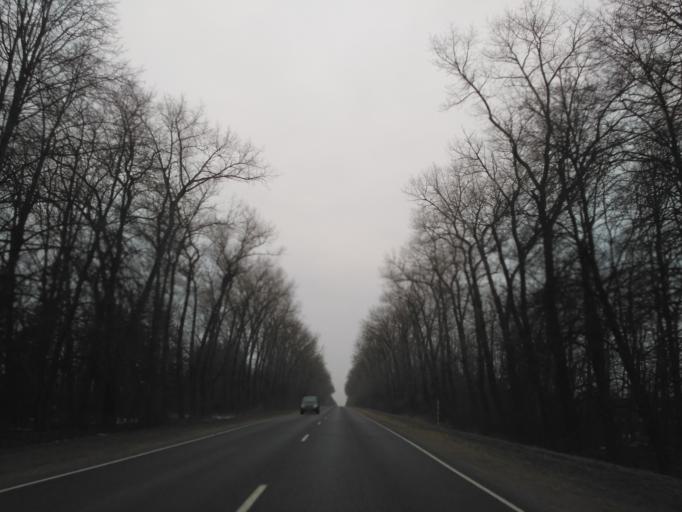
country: BY
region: Minsk
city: Haradzyeya
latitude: 53.3542
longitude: 26.5035
